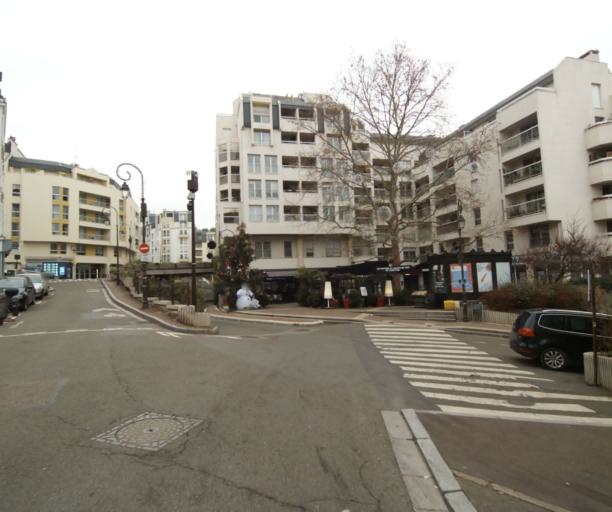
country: FR
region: Ile-de-France
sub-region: Departement des Hauts-de-Seine
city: Saint-Cloud
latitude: 48.8438
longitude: 2.2195
